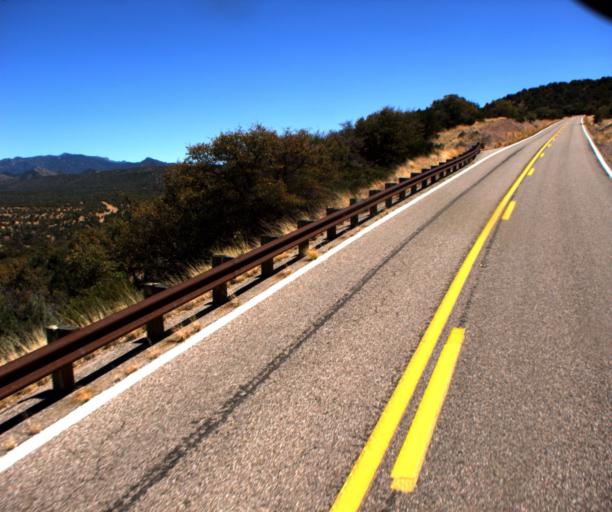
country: US
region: Arizona
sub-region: Cochise County
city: Sierra Vista
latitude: 31.4875
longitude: -110.4854
